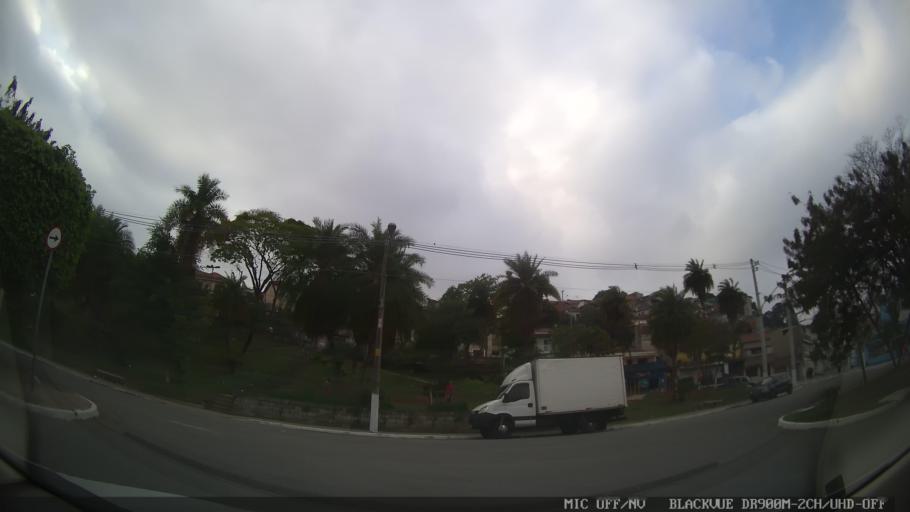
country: BR
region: Sao Paulo
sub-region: Sao Paulo
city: Sao Paulo
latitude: -23.4972
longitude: -46.6022
